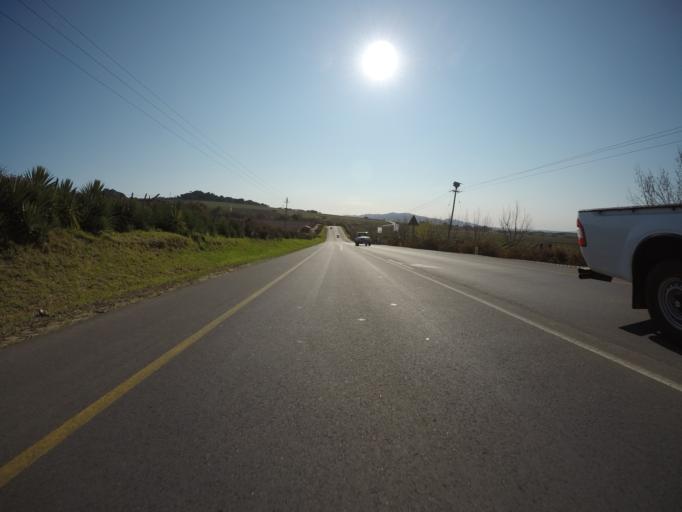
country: ZA
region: Western Cape
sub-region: Cape Winelands District Municipality
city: Noorder-Paarl
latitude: -33.6781
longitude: 18.9406
